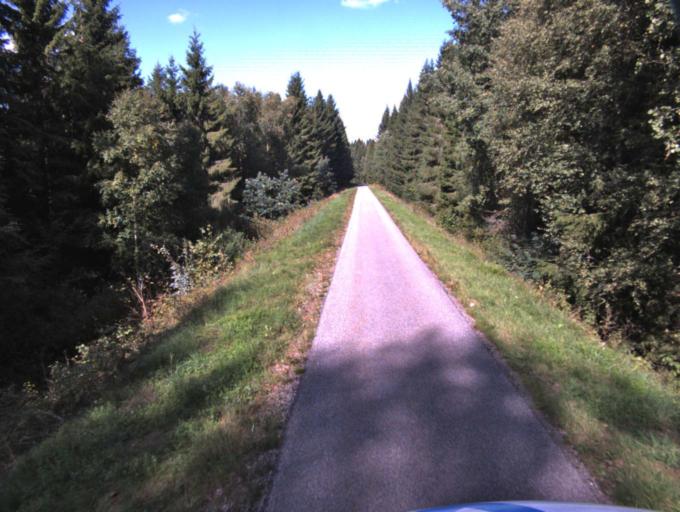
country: SE
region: Vaestra Goetaland
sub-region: Ulricehamns Kommun
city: Ulricehamn
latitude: 57.8269
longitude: 13.3456
